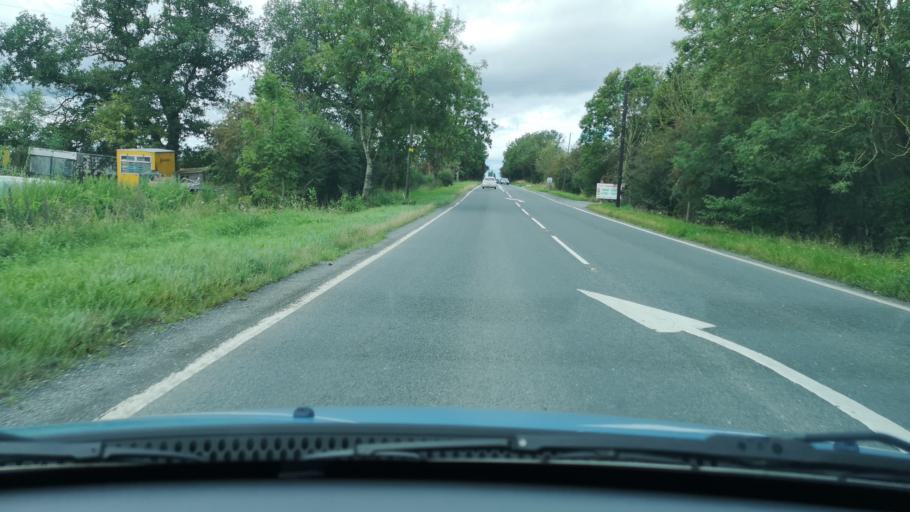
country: GB
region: England
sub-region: City and Borough of Wakefield
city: Low Ackworth
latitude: 53.6329
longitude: -1.3232
